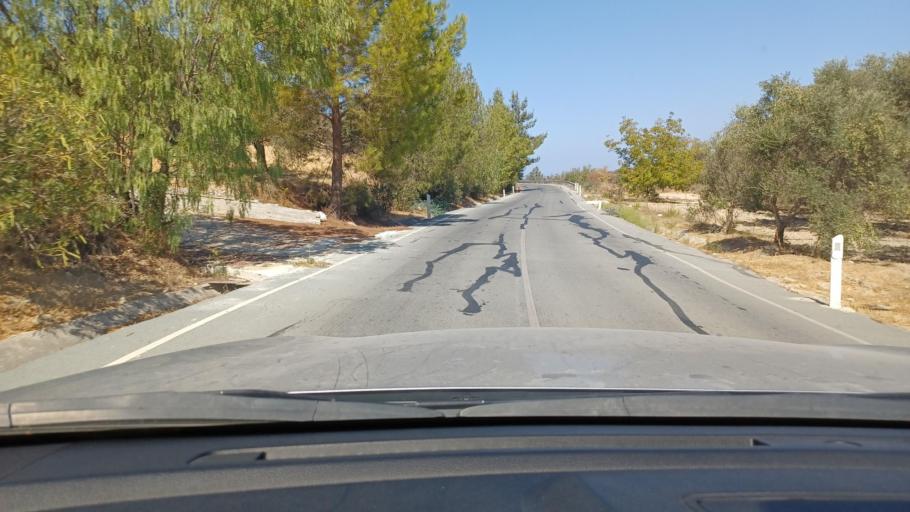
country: CY
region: Pafos
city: Polis
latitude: 35.0055
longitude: 32.4612
